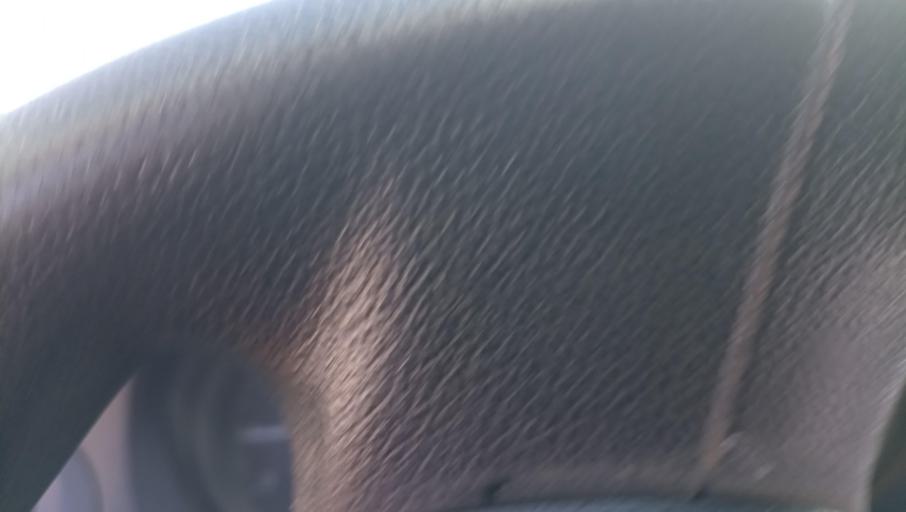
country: TN
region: Tataouine
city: Tataouine
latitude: 32.9835
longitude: 10.3856
